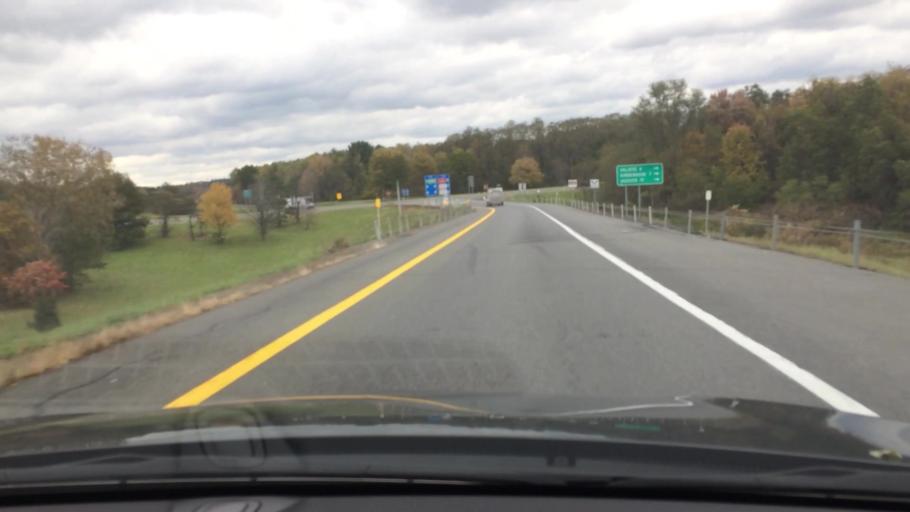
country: US
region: New York
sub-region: Columbia County
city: Niverville
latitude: 42.4899
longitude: -73.6802
